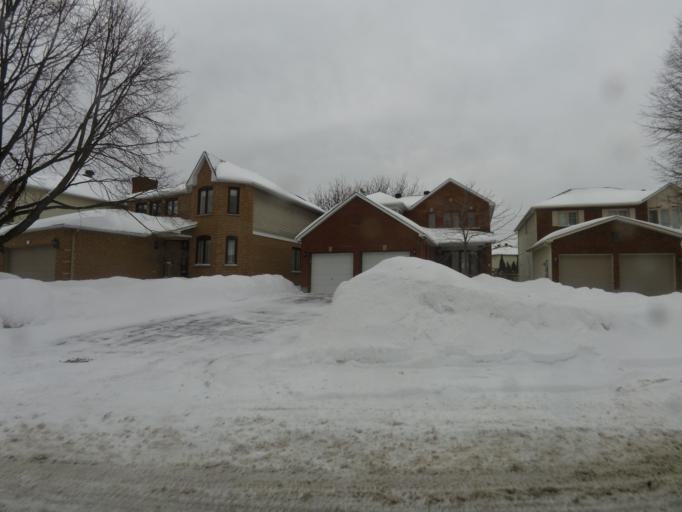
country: CA
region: Ontario
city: Ottawa
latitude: 45.3718
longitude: -75.6192
